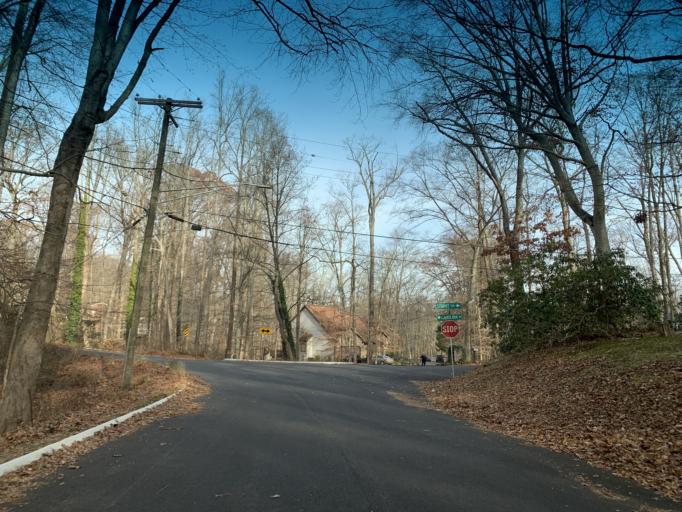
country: US
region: Maryland
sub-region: Harford County
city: South Bel Air
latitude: 39.5238
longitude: -76.3274
